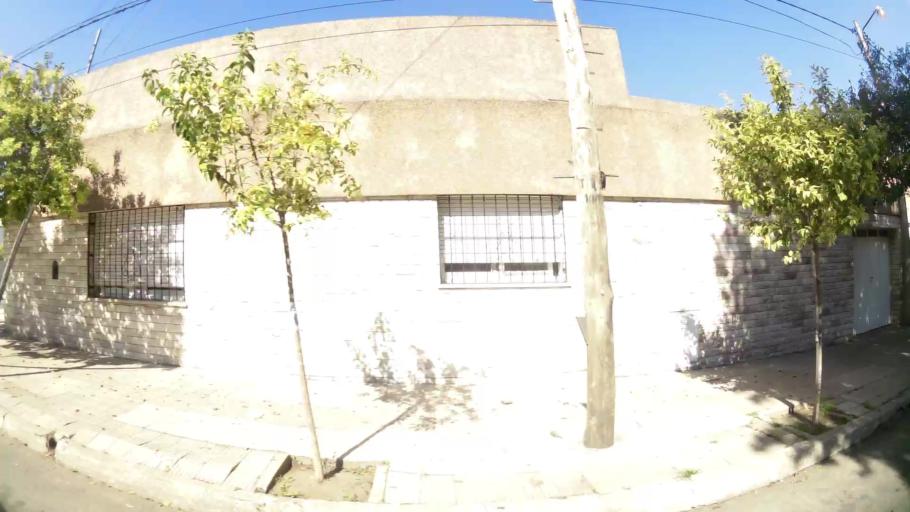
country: AR
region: Cordoba
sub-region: Departamento de Capital
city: Cordoba
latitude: -31.4060
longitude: -64.1561
